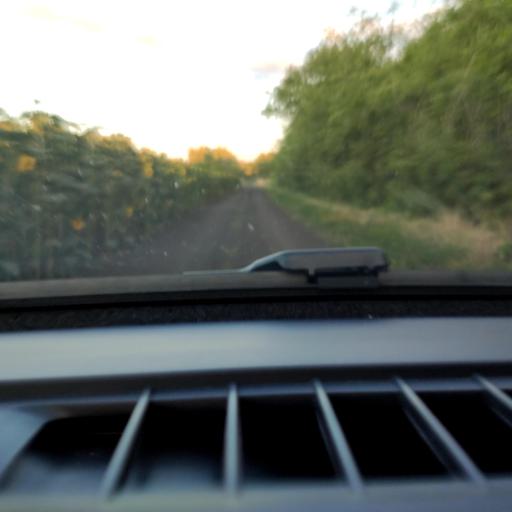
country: RU
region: Voronezj
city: Verkhnyaya Khava
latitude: 51.5935
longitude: 39.8441
